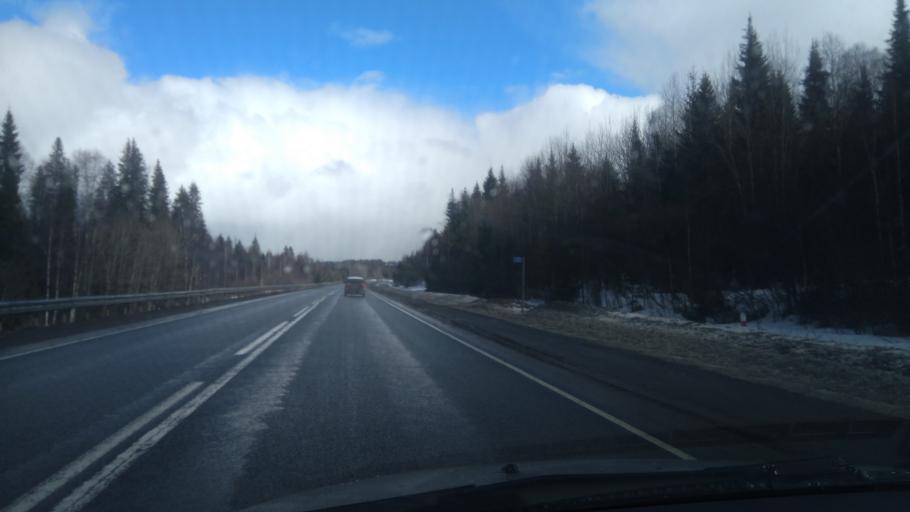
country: RU
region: Sverdlovsk
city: Arti
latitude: 56.7937
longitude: 58.4581
